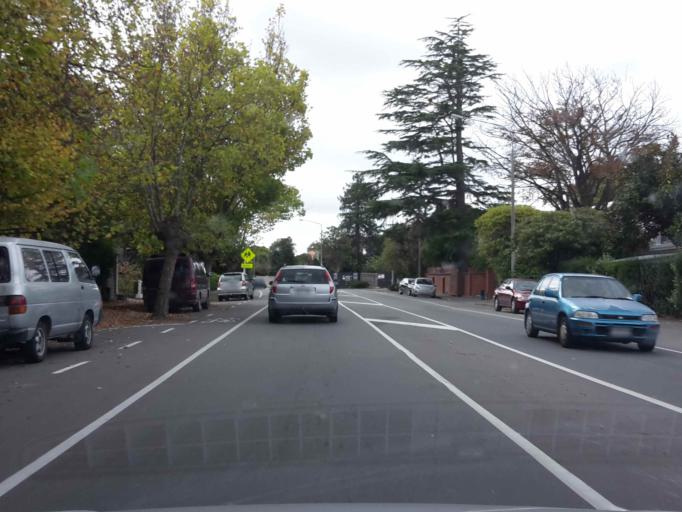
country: NZ
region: Canterbury
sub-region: Christchurch City
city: Christchurch
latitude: -43.5255
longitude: 172.6022
